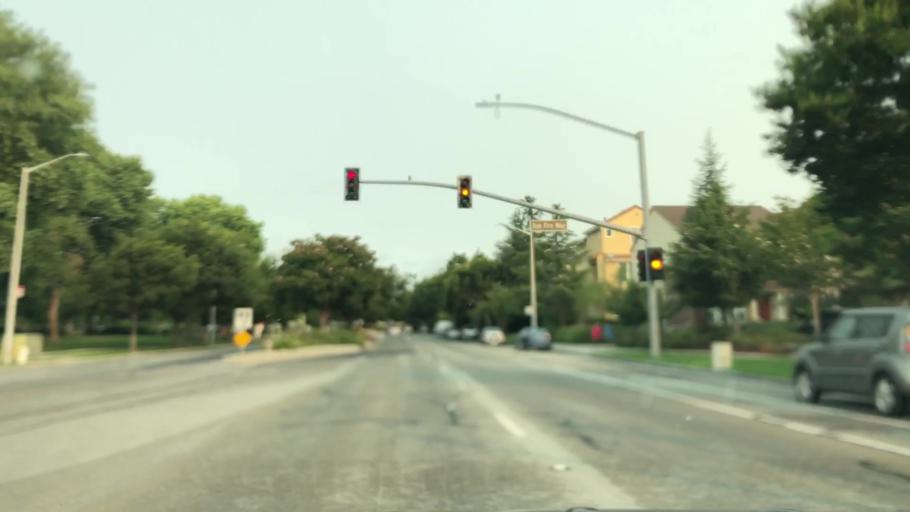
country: US
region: California
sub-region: Santa Clara County
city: Santa Clara
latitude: 37.3950
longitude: -121.9502
